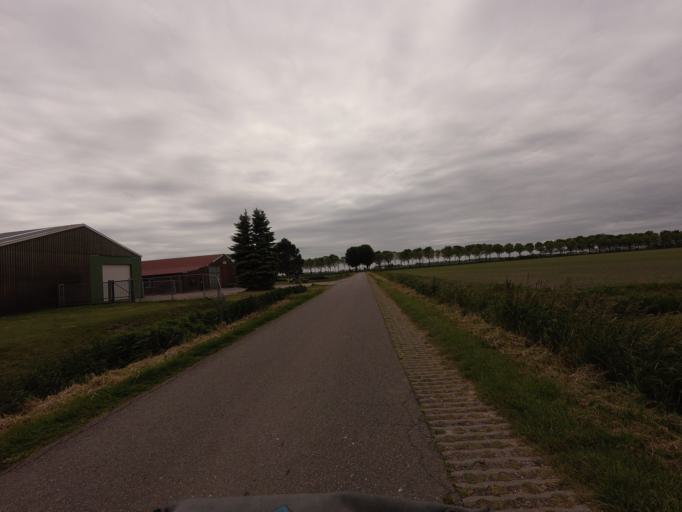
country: NL
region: North Holland
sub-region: Gemeente Medemblik
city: Medemblik
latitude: 52.7547
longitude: 5.1016
